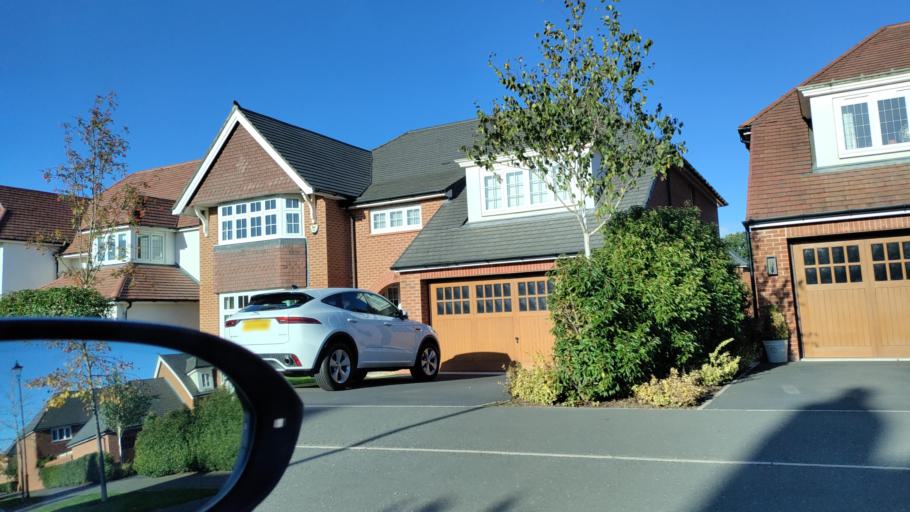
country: GB
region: England
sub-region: Cheshire West and Chester
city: Hartford
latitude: 53.2465
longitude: -2.5514
